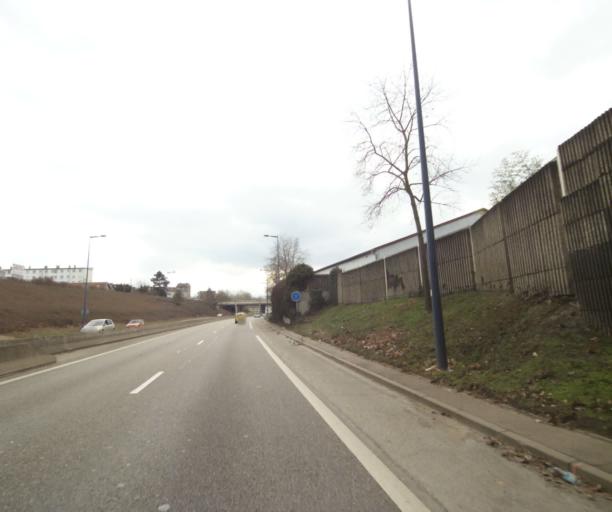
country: FR
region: Lorraine
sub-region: Departement de Meurthe-et-Moselle
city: Jarville-la-Malgrange
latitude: 48.6733
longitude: 6.1956
